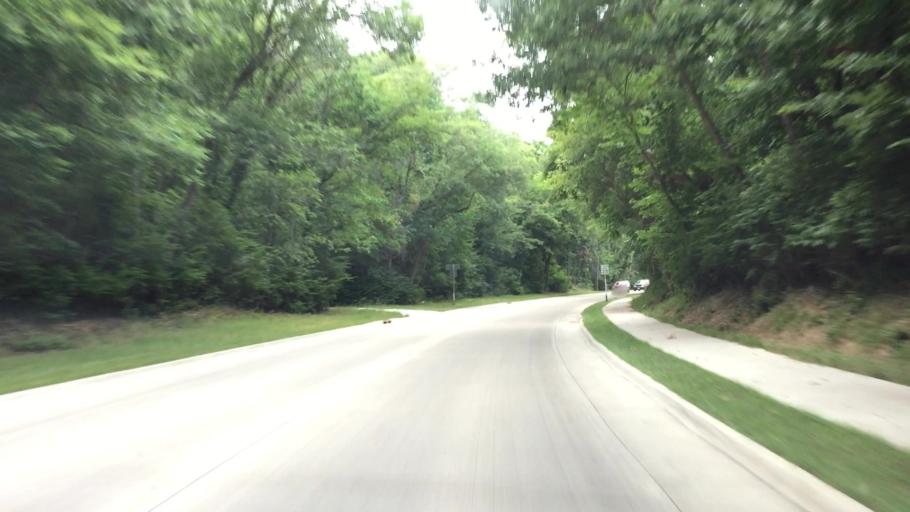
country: US
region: Iowa
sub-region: Lee County
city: Fort Madison
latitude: 40.6376
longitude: -91.3244
